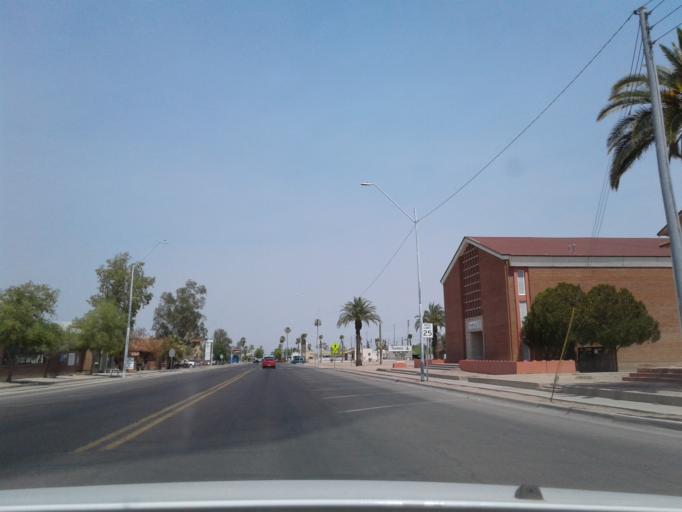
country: US
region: Arizona
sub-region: Pinal County
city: Casa Grande
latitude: 32.8747
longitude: -111.7490
